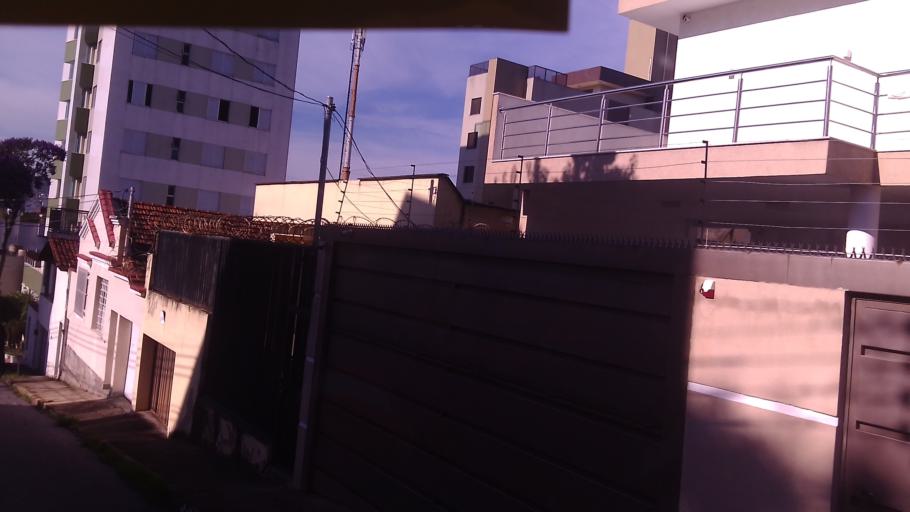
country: BR
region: Minas Gerais
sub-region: Belo Horizonte
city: Belo Horizonte
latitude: -19.9162
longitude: -43.9726
